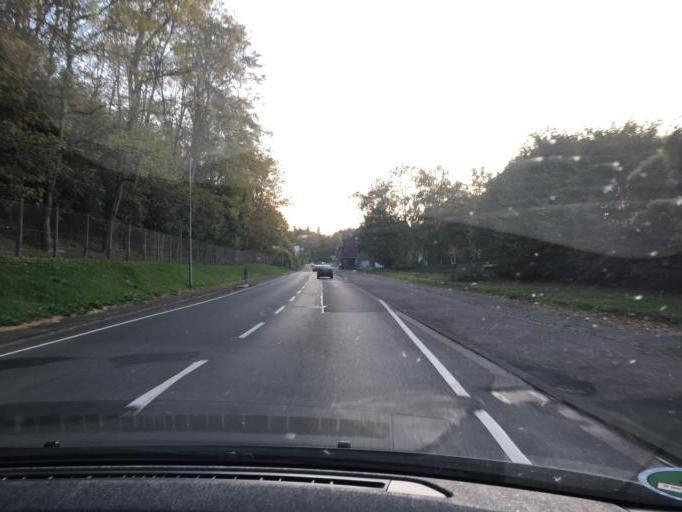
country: DE
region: North Rhine-Westphalia
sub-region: Regierungsbezirk Koln
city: Hurth
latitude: 50.8638
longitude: 6.8615
